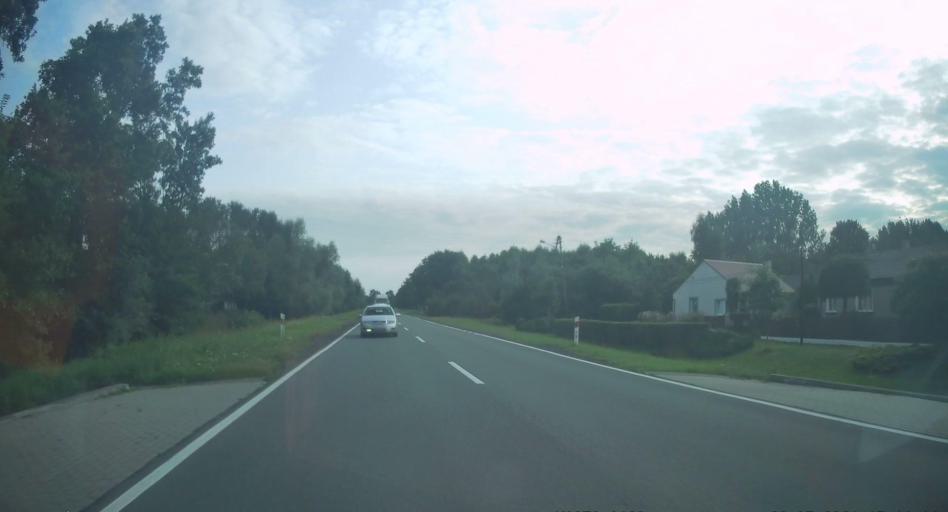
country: PL
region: Silesian Voivodeship
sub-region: Powiat czestochowski
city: Klomnice
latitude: 50.9344
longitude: 19.3835
